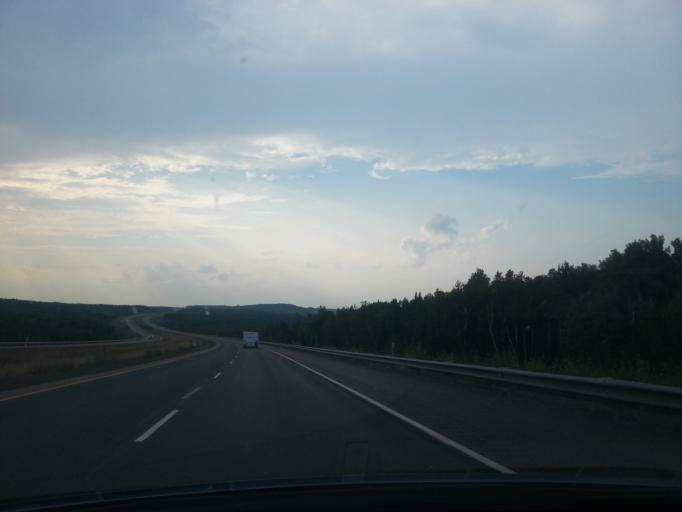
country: CA
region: New Brunswick
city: Harrison Brook
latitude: 47.2855
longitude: -68.0311
